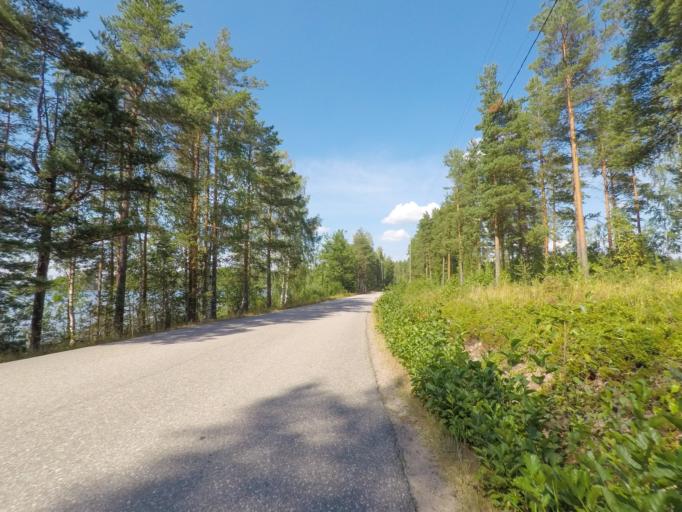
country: FI
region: Southern Savonia
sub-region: Mikkeli
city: Puumala
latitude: 61.4322
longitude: 28.1702
